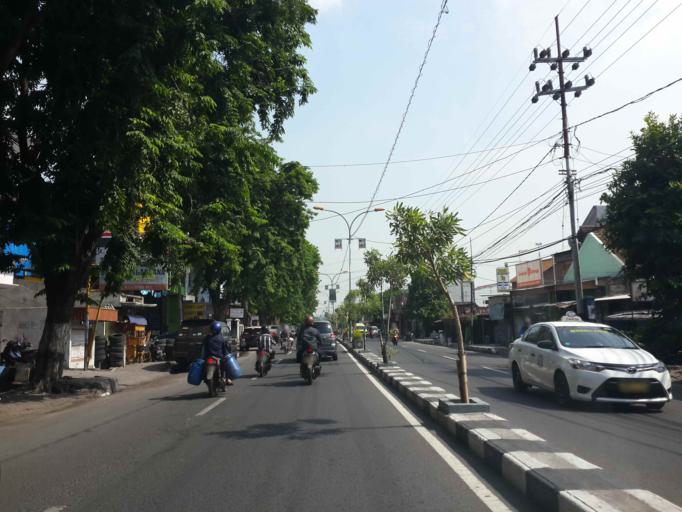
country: ID
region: East Java
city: Kebomas
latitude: -7.1744
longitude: 112.6523
